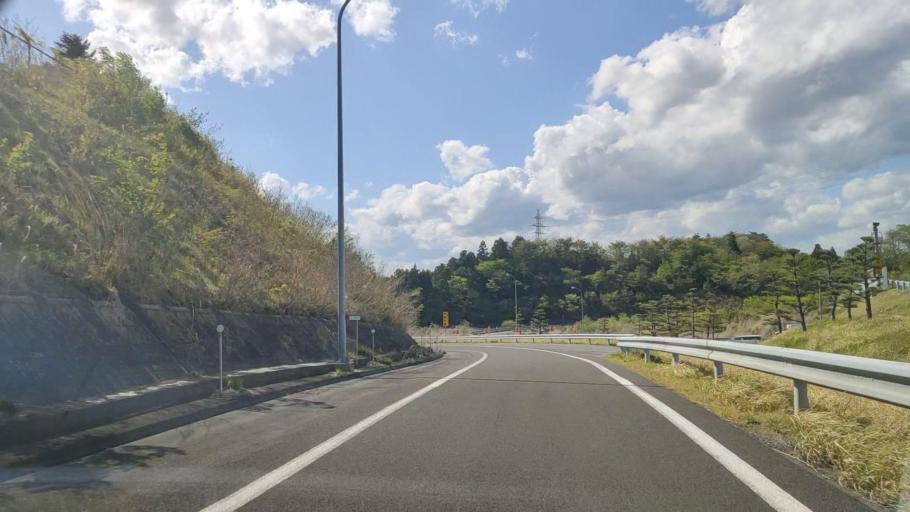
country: JP
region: Miyagi
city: Yamoto
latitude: 38.4107
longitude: 141.1376
